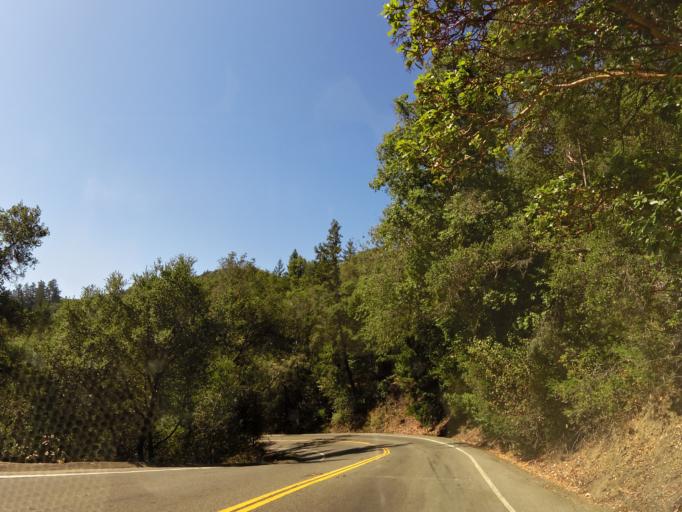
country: US
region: California
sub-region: Sonoma County
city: Cloverdale
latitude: 38.8425
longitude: -123.0631
